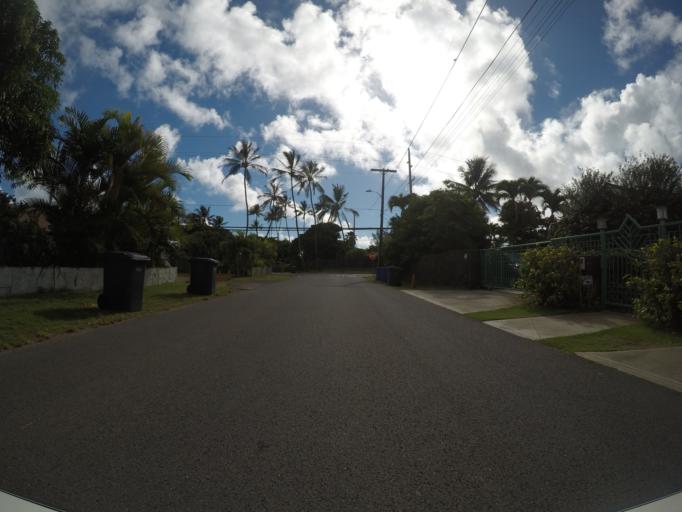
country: US
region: Hawaii
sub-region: Honolulu County
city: Kailua
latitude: 21.4027
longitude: -157.7400
